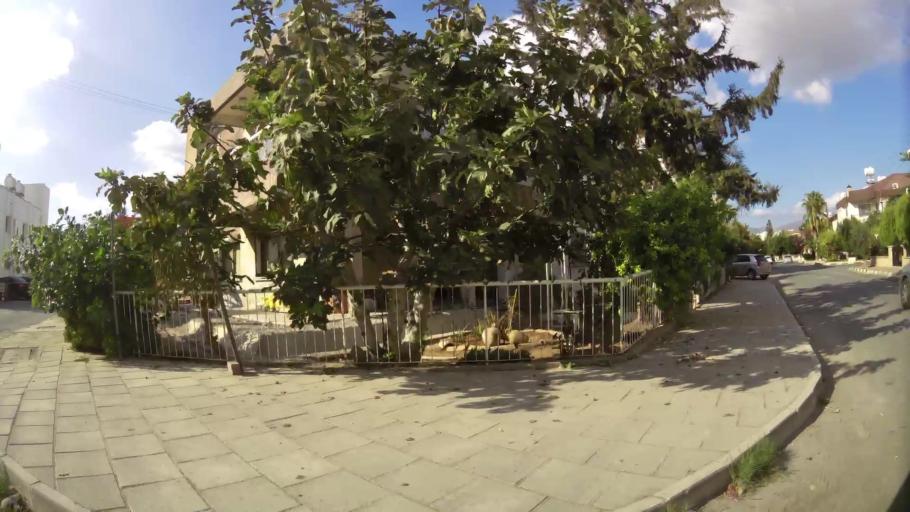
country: CY
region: Lefkosia
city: Nicosia
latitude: 35.1937
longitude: 33.3604
